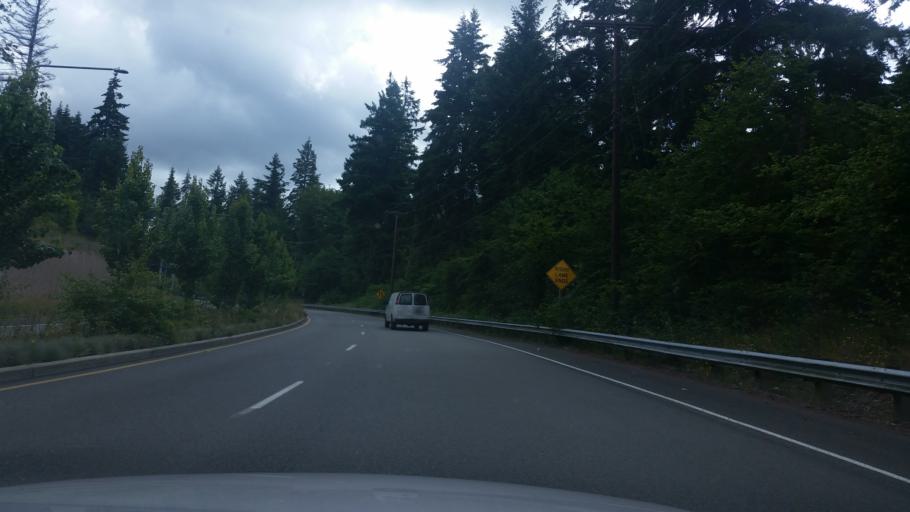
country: US
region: Washington
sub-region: King County
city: Redmond
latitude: 47.6876
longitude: -122.0787
